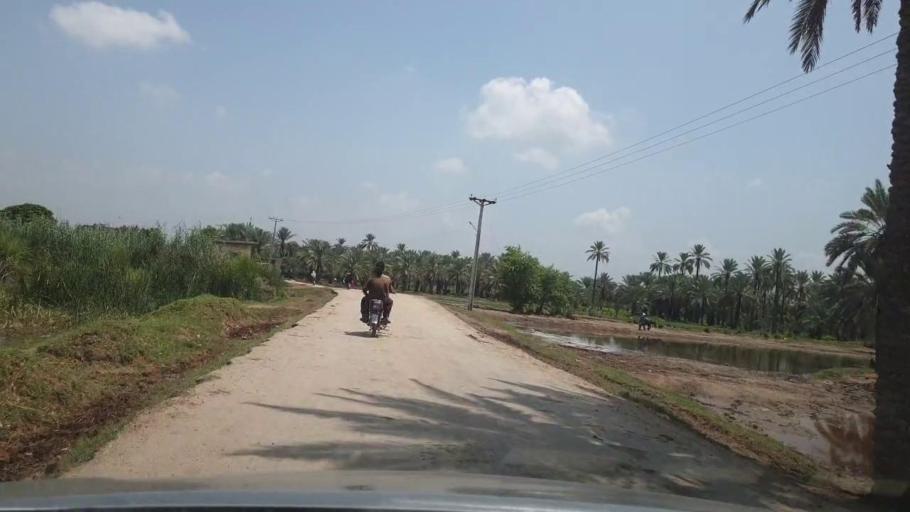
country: PK
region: Sindh
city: Pir jo Goth
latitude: 27.6006
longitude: 68.6032
